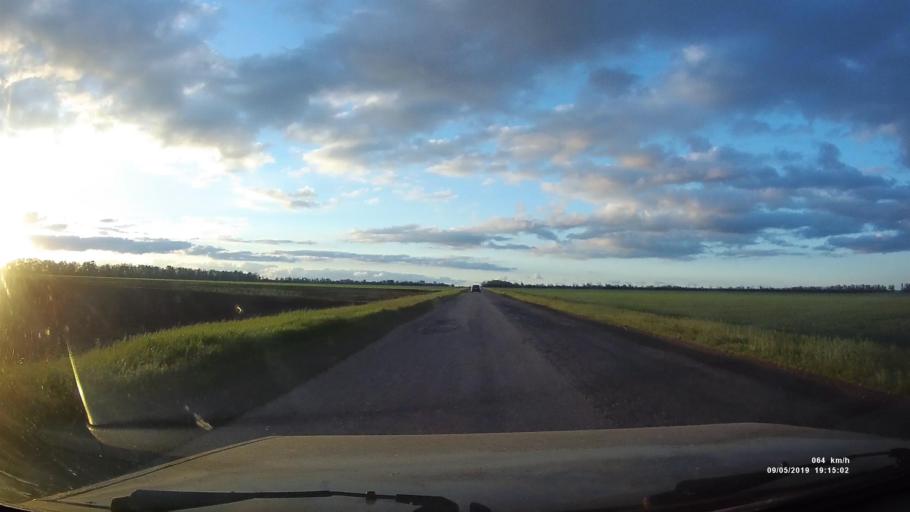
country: RU
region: Krasnodarskiy
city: Kanelovskaya
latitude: 46.7651
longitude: 39.2124
